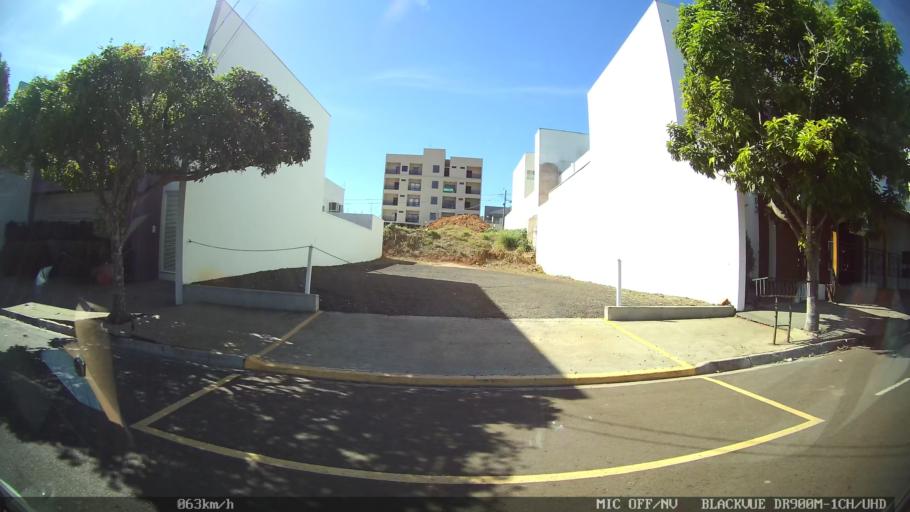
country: BR
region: Sao Paulo
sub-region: Franca
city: Franca
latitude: -20.5392
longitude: -47.3755
